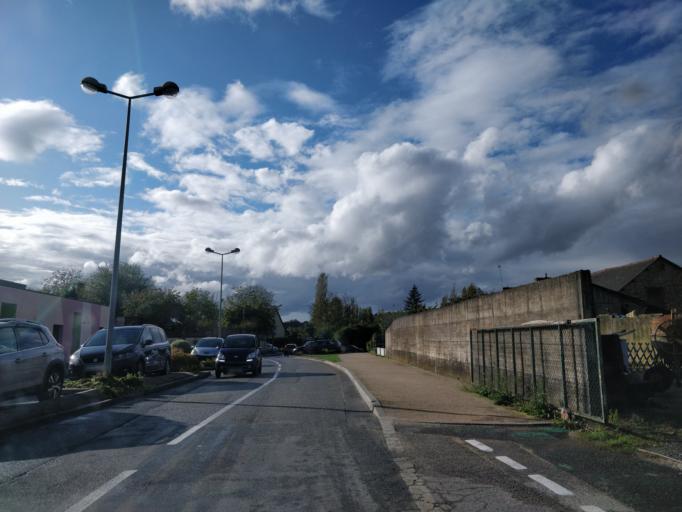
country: FR
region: Brittany
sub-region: Departement d'Ille-et-Vilaine
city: Servon-sur-Vilaine
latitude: 48.1230
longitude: -1.4578
